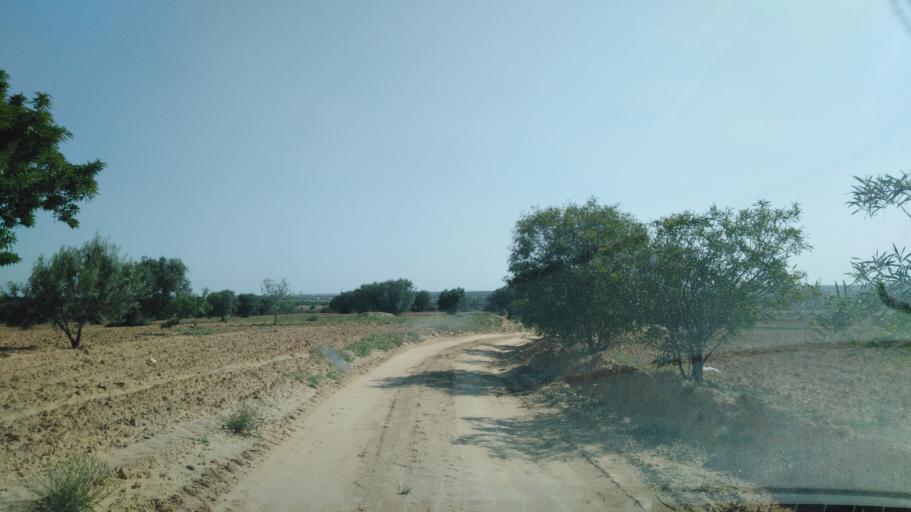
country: TN
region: Safaqis
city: Bi'r `Ali Bin Khalifah
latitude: 34.7850
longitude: 10.3696
